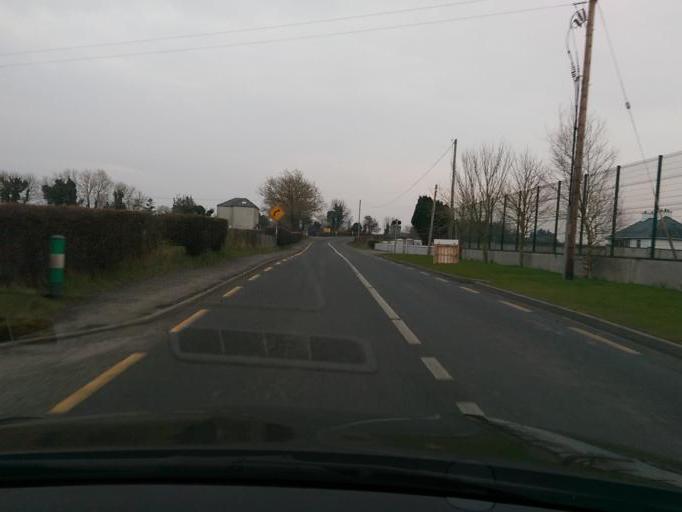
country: IE
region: Leinster
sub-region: An Longfort
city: Ballymahon
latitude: 53.5340
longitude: -7.7922
